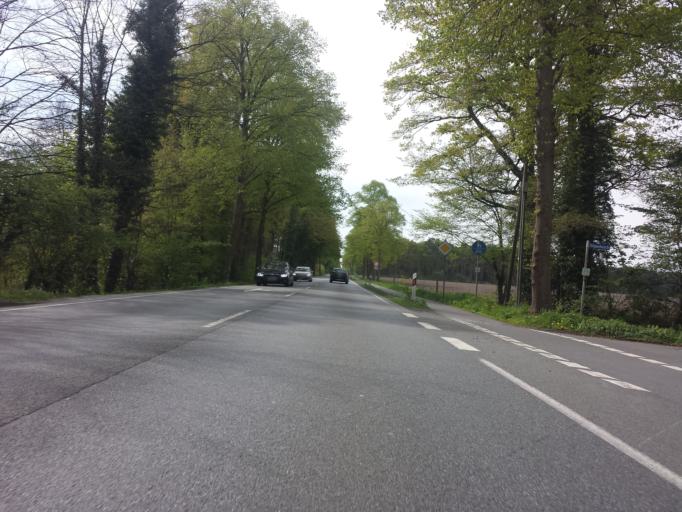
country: DE
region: North Rhine-Westphalia
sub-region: Regierungsbezirk Detmold
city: Guetersloh
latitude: 51.8713
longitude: 8.3451
